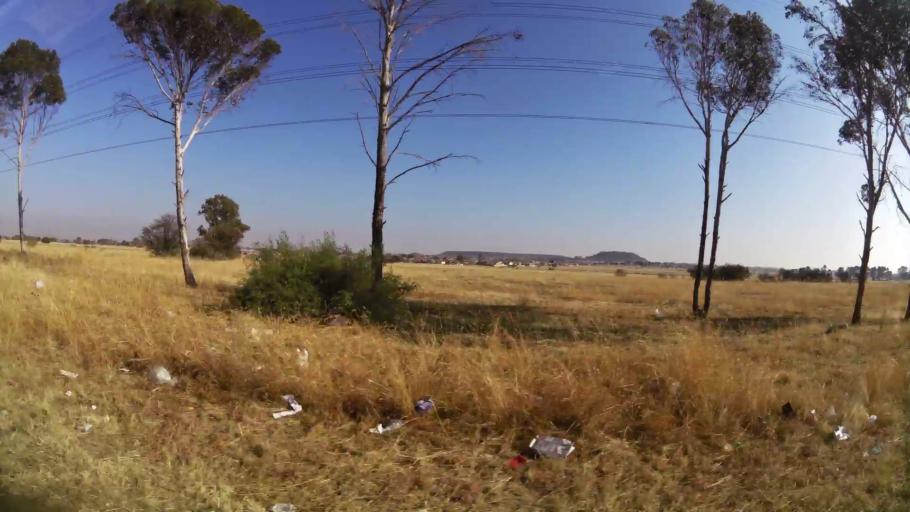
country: ZA
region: Orange Free State
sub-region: Mangaung Metropolitan Municipality
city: Bloemfontein
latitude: -29.1835
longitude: 26.1877
